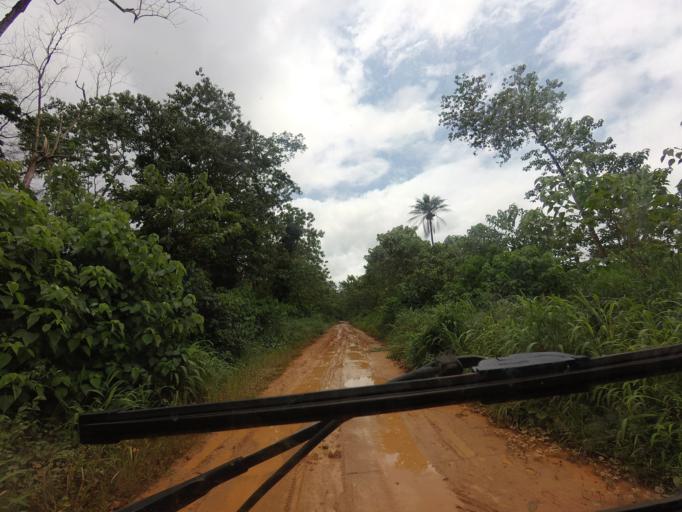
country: SL
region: Eastern Province
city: Tombodu
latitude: 8.1383
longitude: -10.6554
